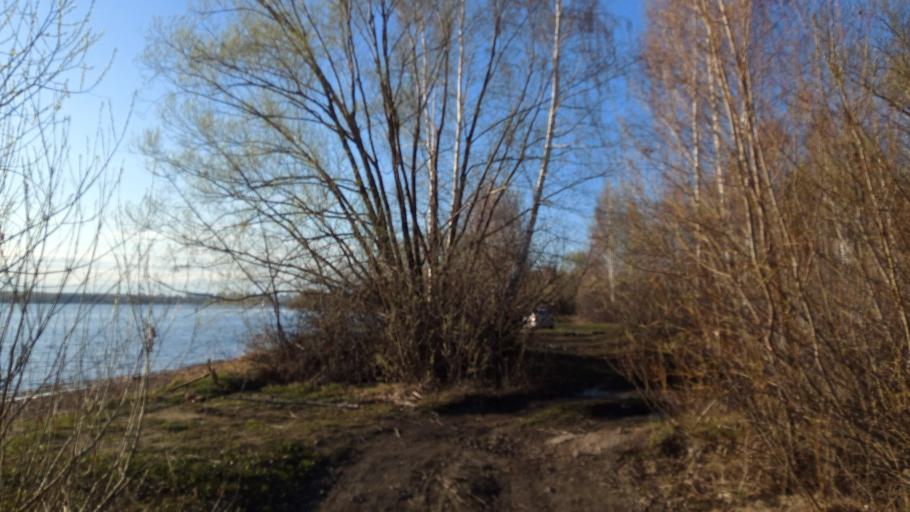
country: RU
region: Chelyabinsk
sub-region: Gorod Chelyabinsk
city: Chelyabinsk
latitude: 55.1327
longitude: 61.3276
